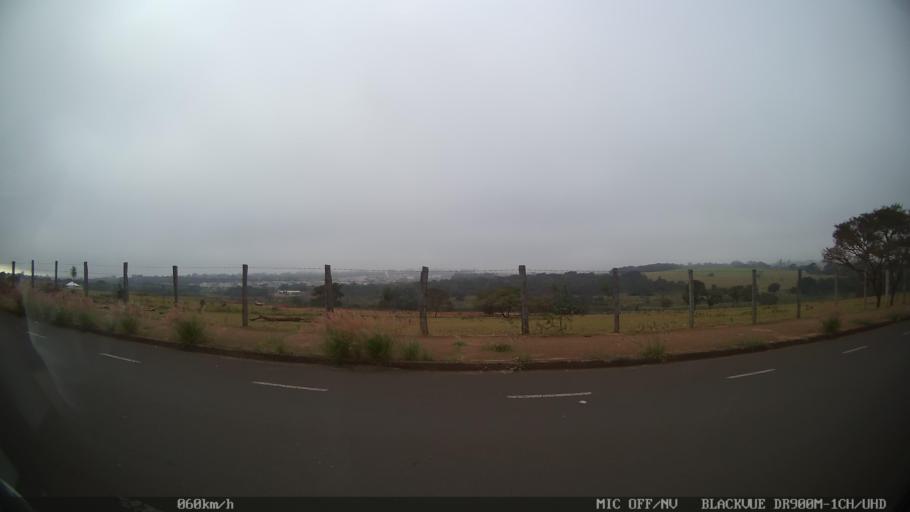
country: BR
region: Sao Paulo
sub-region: Sao Jose Do Rio Preto
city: Sao Jose do Rio Preto
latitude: -20.8542
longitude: -49.3709
